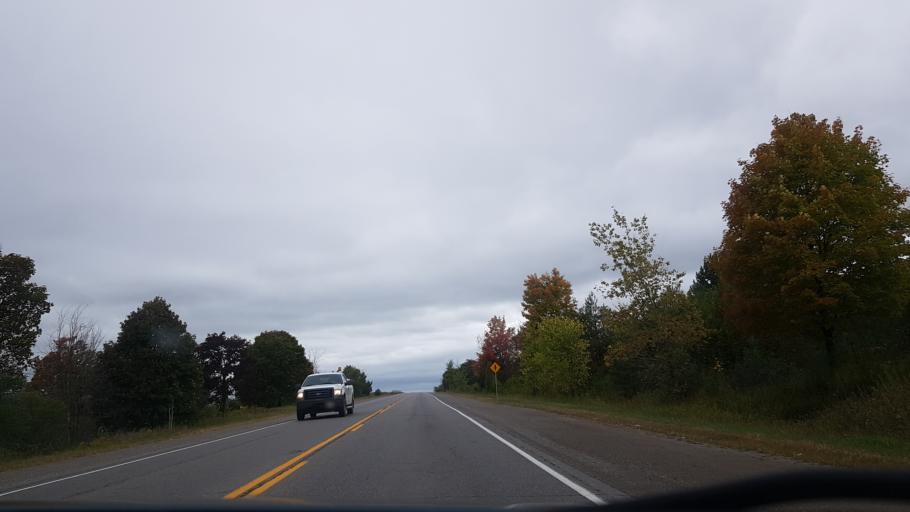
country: CA
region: Ontario
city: Peterborough
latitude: 44.2617
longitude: -78.3752
